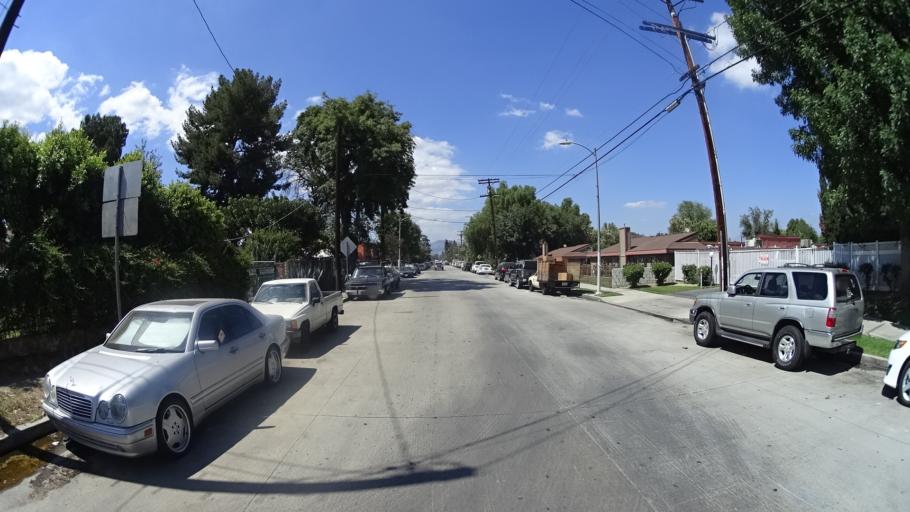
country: US
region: California
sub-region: Los Angeles County
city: Van Nuys
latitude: 34.2229
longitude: -118.4632
